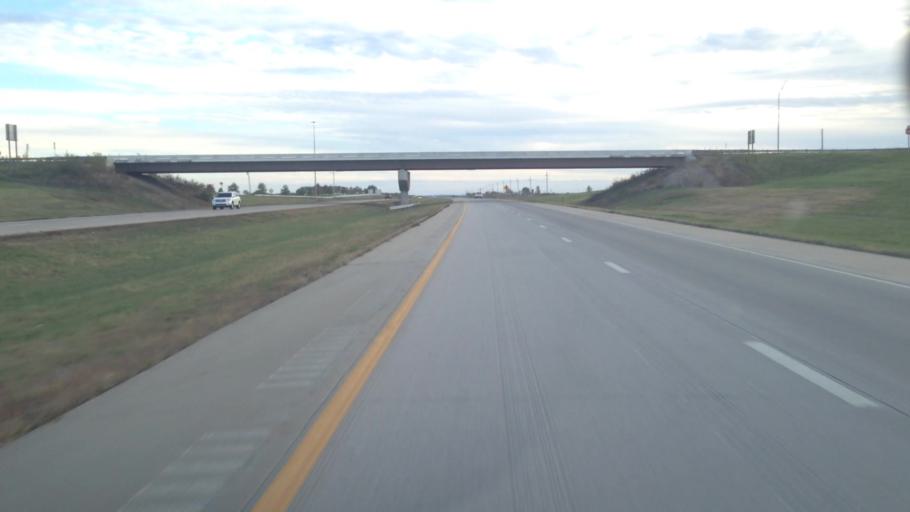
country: US
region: Kansas
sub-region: Douglas County
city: Baldwin City
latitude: 38.8346
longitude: -95.2691
